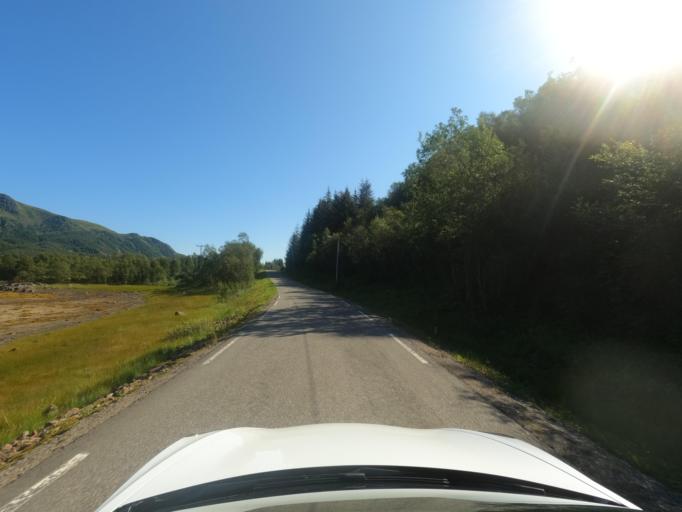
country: NO
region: Nordland
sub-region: Hadsel
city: Stokmarknes
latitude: 68.2989
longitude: 15.0432
